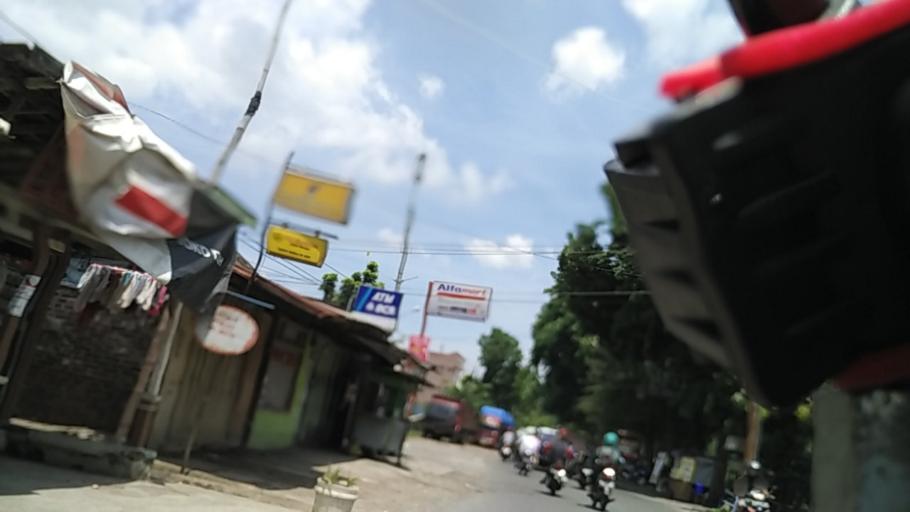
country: ID
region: Central Java
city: Semarang
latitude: -7.0083
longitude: 110.3876
